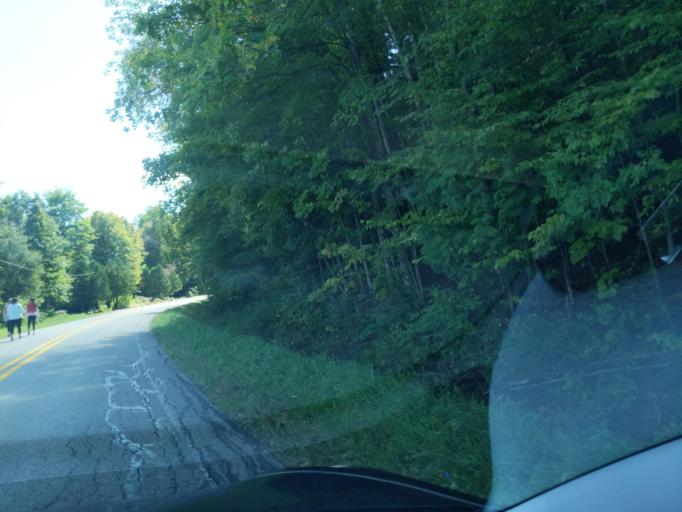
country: US
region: Michigan
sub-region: Antrim County
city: Elk Rapids
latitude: 44.9580
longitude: -85.3239
